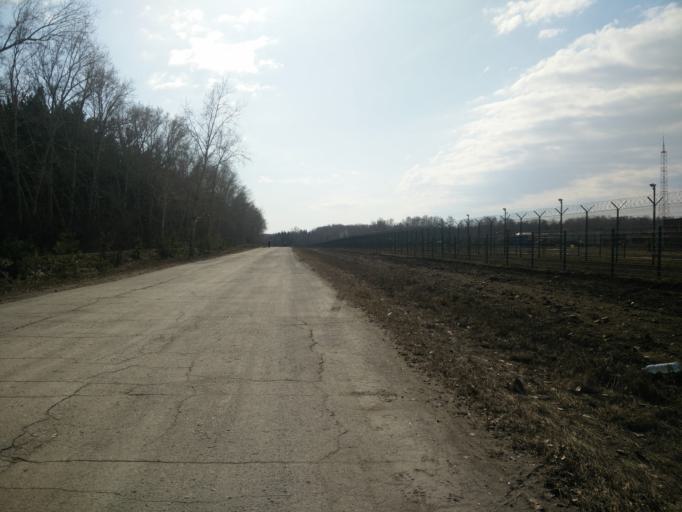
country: RU
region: Novosibirsk
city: Berdsk
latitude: 54.7629
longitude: 83.0761
